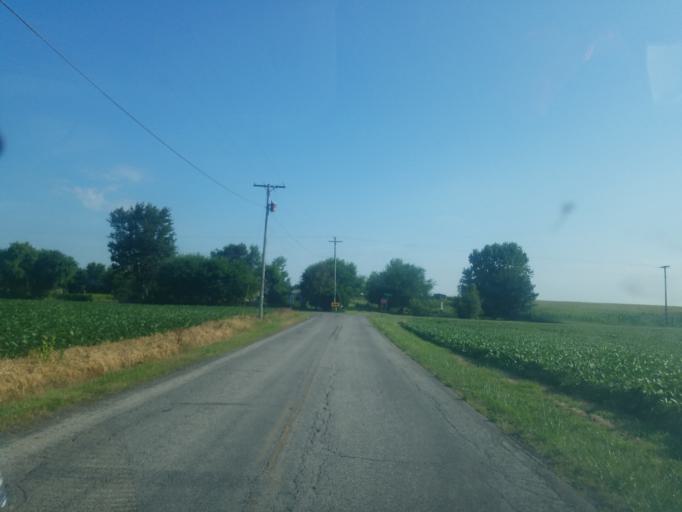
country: US
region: Ohio
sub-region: Richland County
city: Shelby
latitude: 40.8351
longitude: -82.6963
